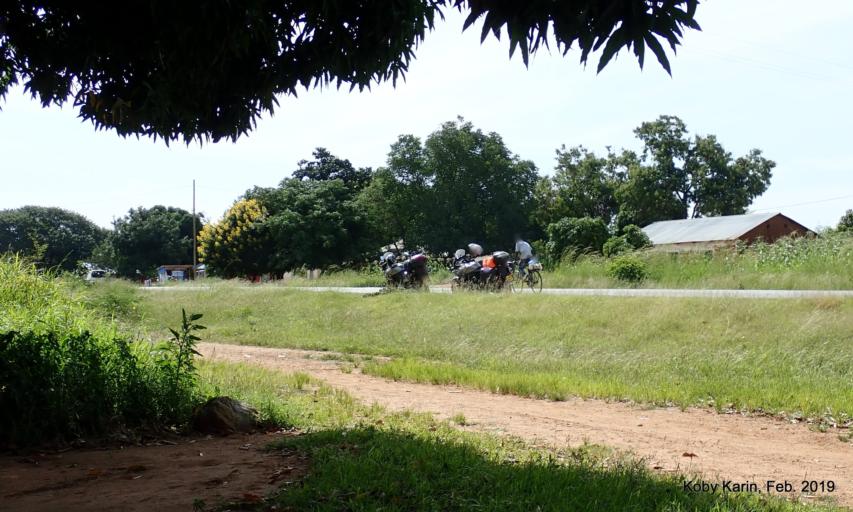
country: TZ
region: Tabora
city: Nzega
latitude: -4.2096
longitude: 33.3004
